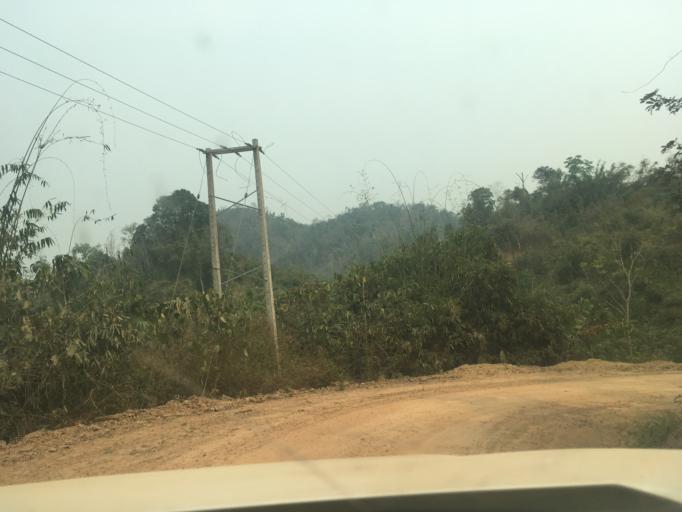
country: VN
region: Huyen Dien Bien
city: Dien Bien Phu
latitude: 21.5414
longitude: 102.8137
